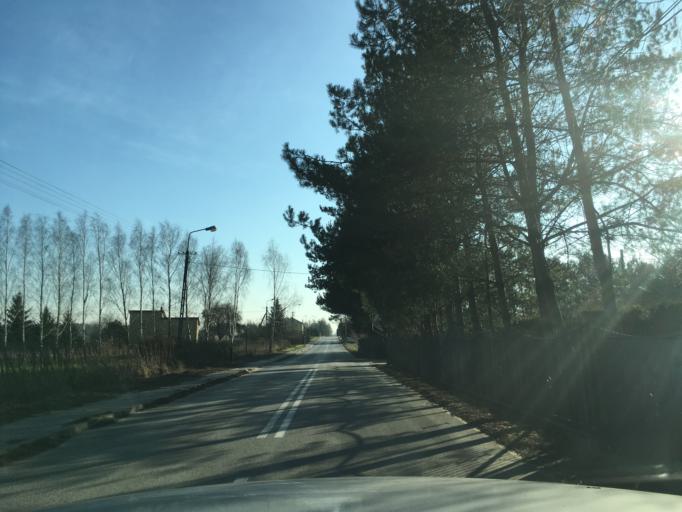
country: PL
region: Masovian Voivodeship
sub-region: Powiat pruszkowski
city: Nadarzyn
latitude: 52.0488
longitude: 20.8258
